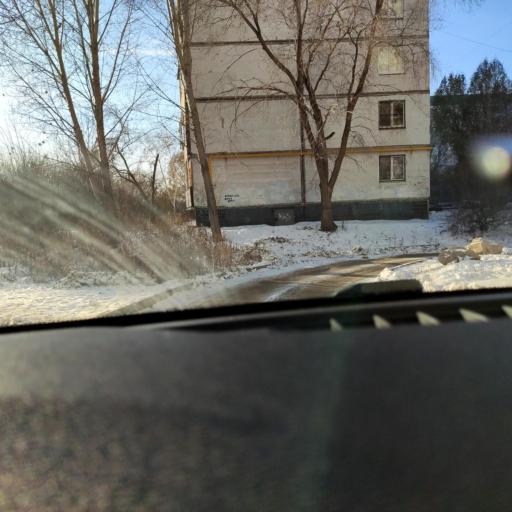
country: RU
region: Samara
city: Samara
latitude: 53.1892
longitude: 50.1476
